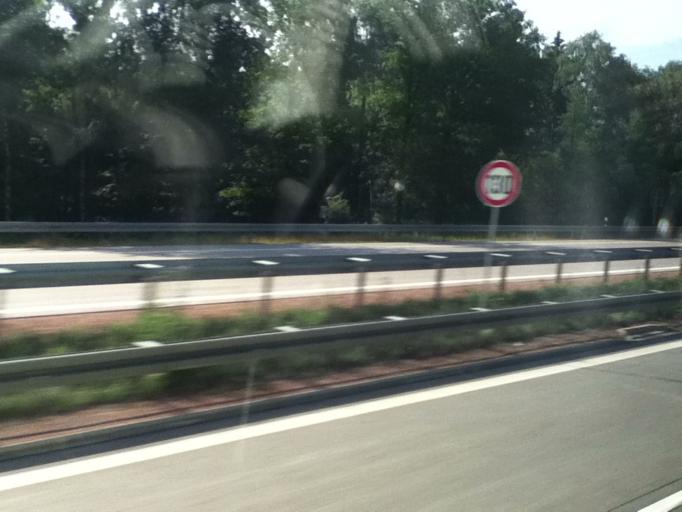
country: DE
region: Saxony
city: Limbach-Oberfrohna
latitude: 50.8403
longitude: 12.7972
